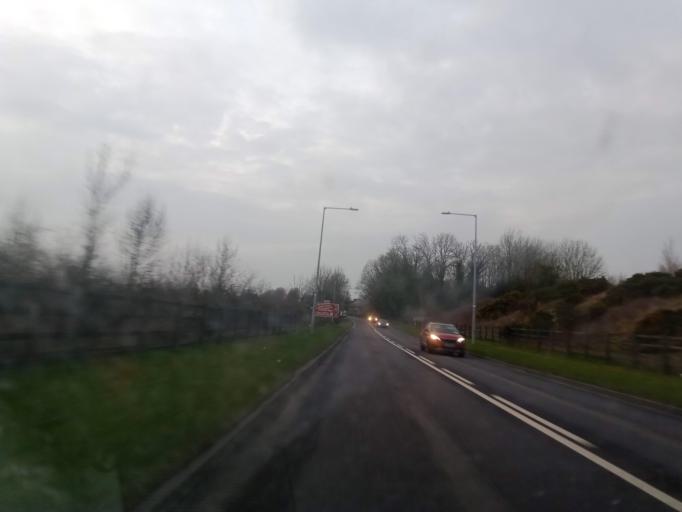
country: IE
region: Leinster
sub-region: Kilkenny
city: Kilkenny
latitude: 52.6789
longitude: -7.2533
